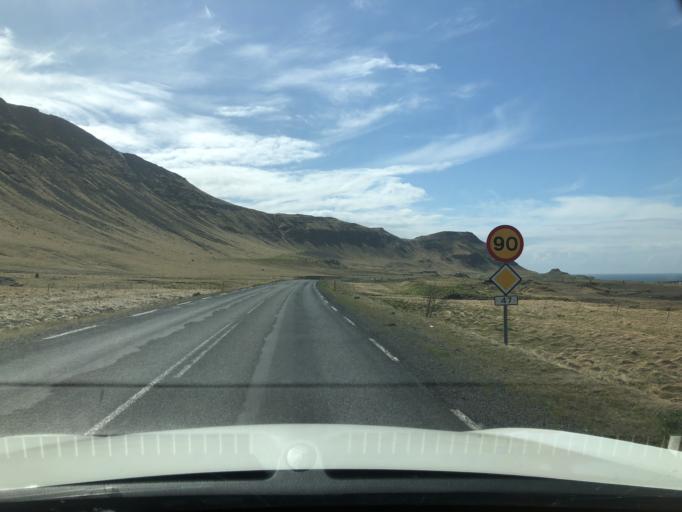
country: IS
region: Capital Region
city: Mosfellsbaer
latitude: 64.2948
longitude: -21.7939
